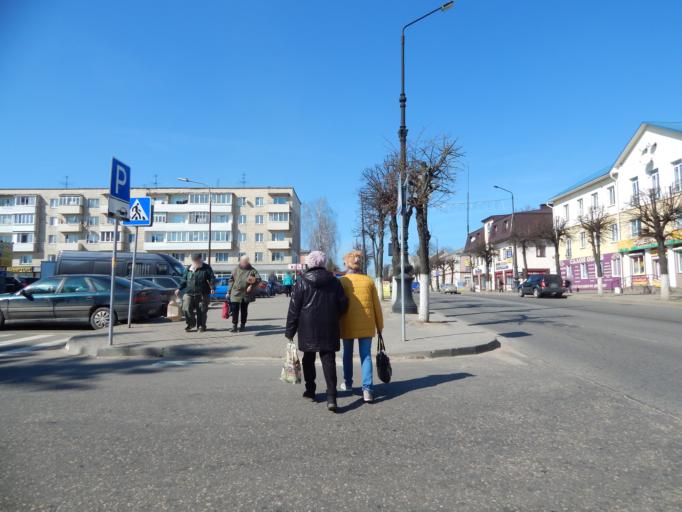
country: BY
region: Minsk
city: Horad Barysaw
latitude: 54.2217
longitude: 28.5227
